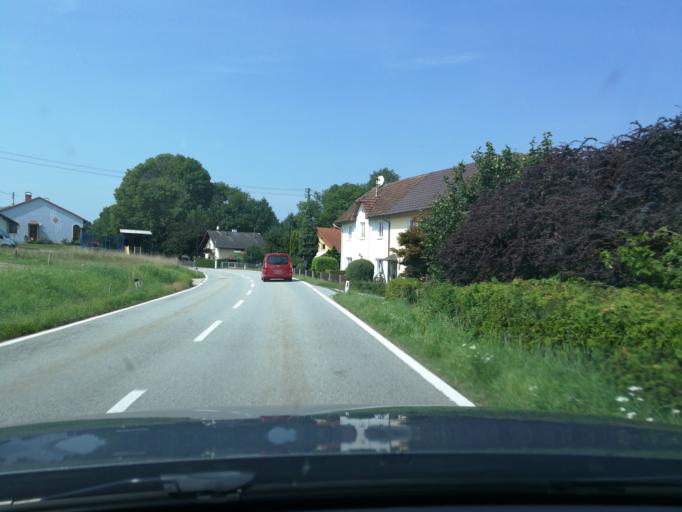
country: DE
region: Bavaria
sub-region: Lower Bavaria
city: Obernzell
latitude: 48.3627
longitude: 13.6765
